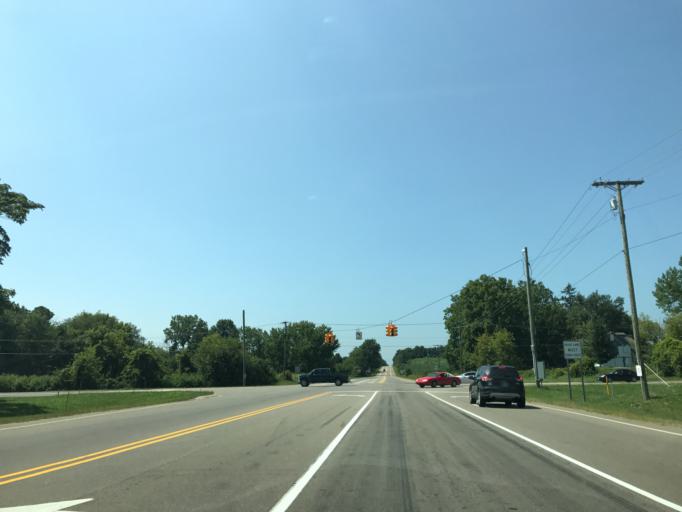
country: US
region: Michigan
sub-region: Berrien County
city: Buchanan
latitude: 41.8051
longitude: -86.3575
